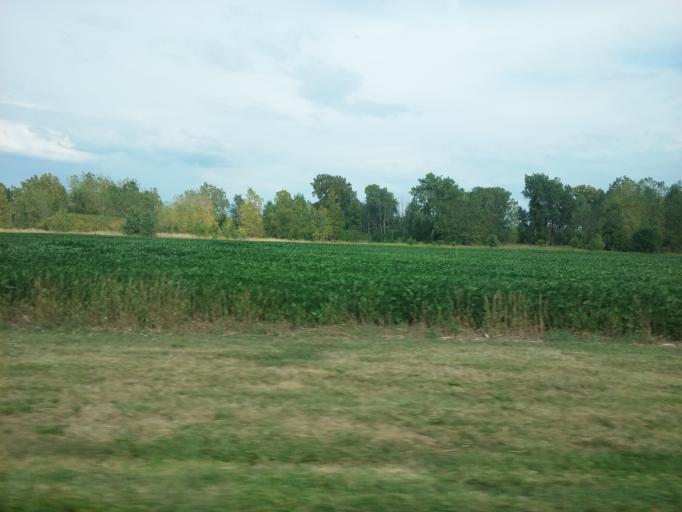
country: US
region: Ohio
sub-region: Hancock County
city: McComb
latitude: 41.1944
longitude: -83.7844
